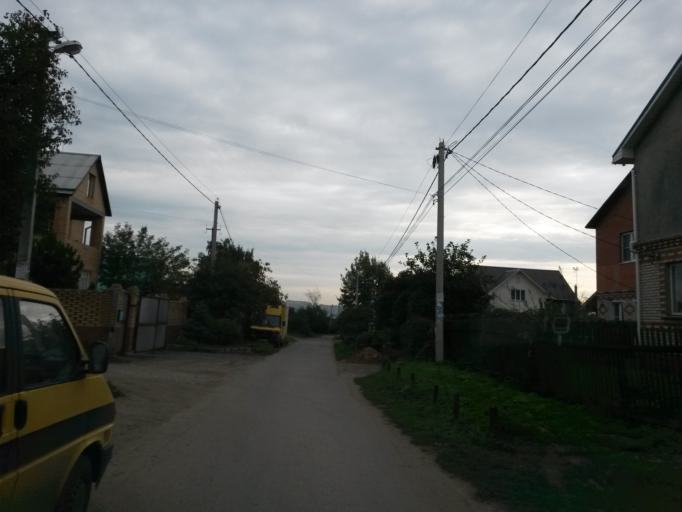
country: RU
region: Moskovskaya
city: Alekseyevka
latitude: 55.6062
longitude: 37.8056
